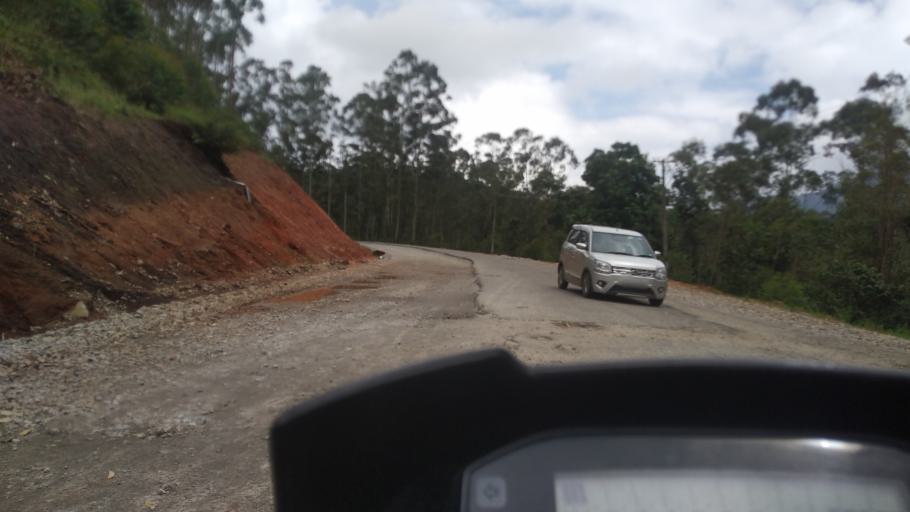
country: IN
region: Kerala
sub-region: Idukki
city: Munnar
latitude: 10.0709
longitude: 77.0958
